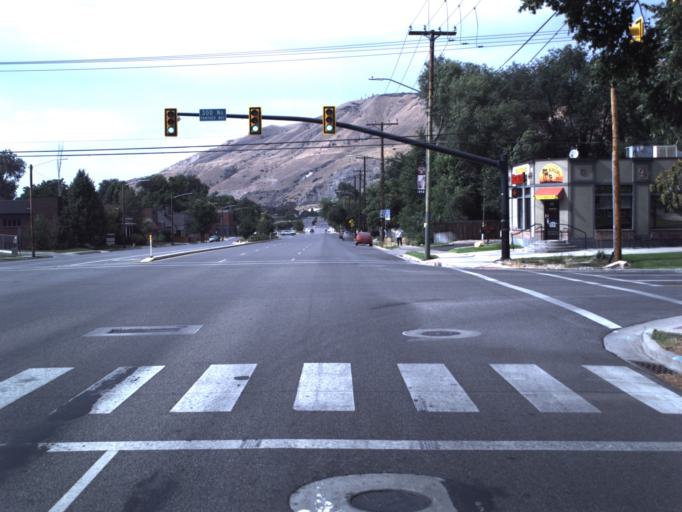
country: US
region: Utah
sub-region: Salt Lake County
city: Salt Lake City
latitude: 40.7756
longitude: -111.8996
